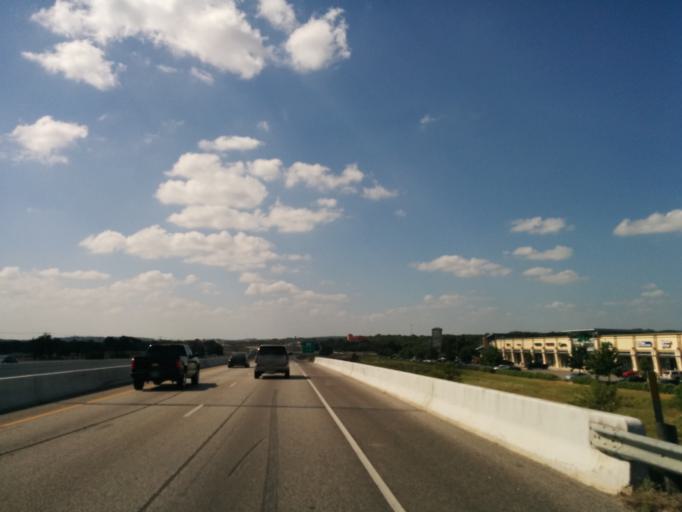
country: US
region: Texas
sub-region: Bexar County
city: Cross Mountain
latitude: 29.6668
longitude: -98.6316
